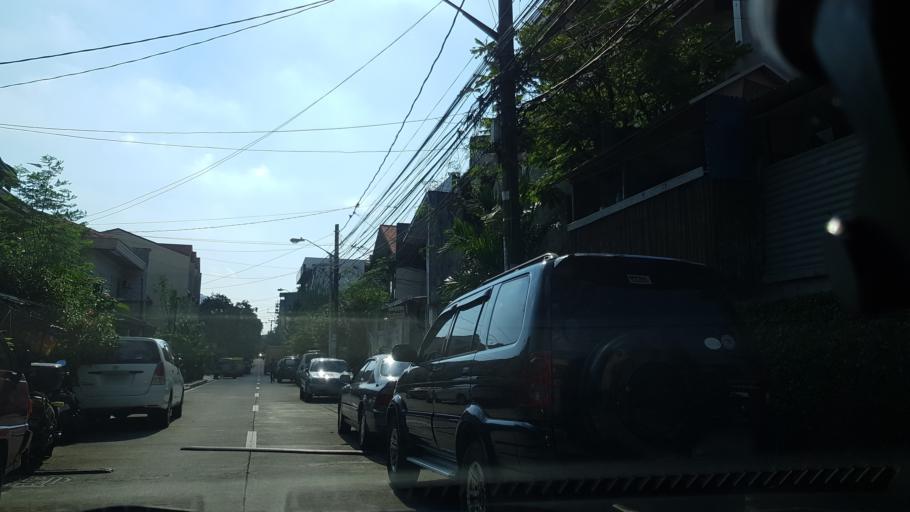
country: PH
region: Metro Manila
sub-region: Quezon City
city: Quezon City
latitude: 14.6294
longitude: 121.0430
